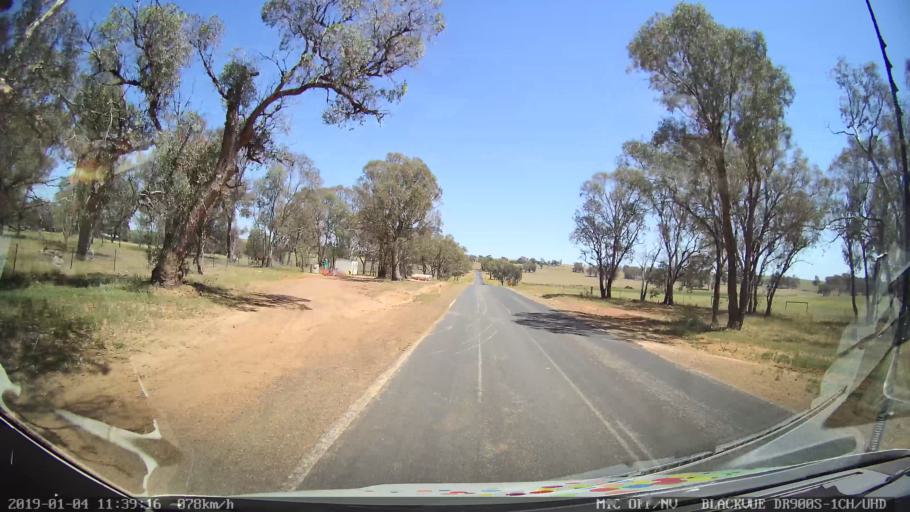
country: AU
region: New South Wales
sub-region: Cabonne
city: Molong
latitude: -33.0149
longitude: 148.7971
